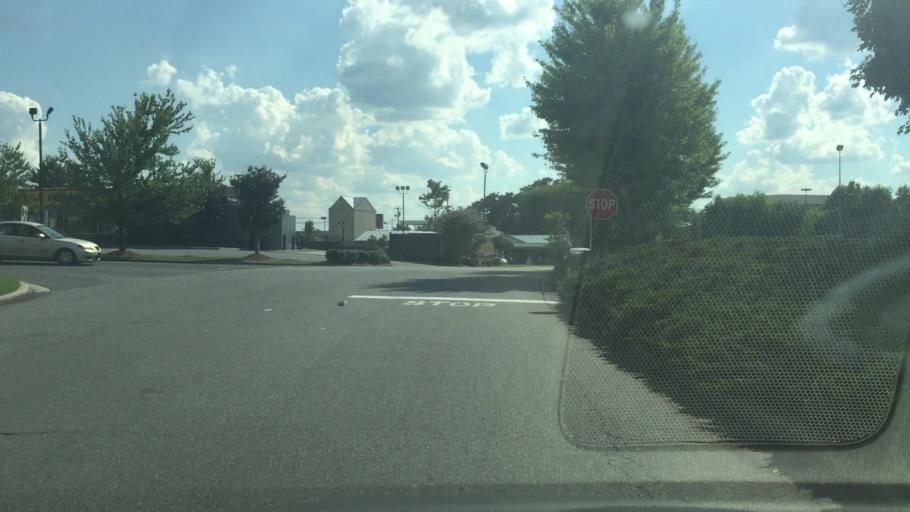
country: US
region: North Carolina
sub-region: Cabarrus County
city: Concord
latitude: 35.3970
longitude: -80.6114
